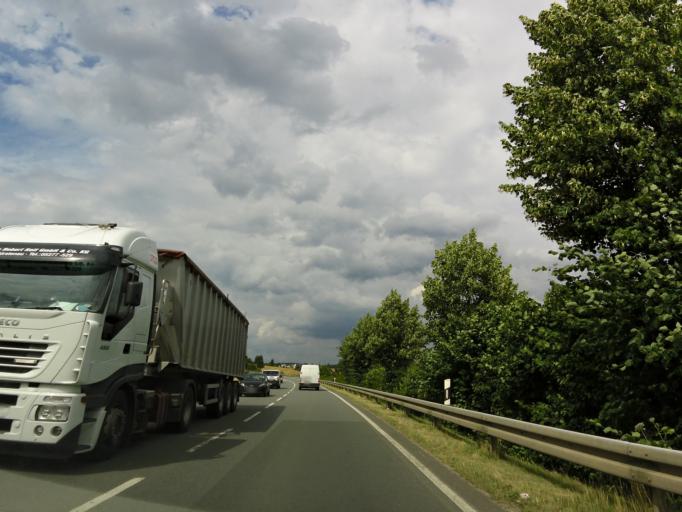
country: DE
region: North Rhine-Westphalia
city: Beverungen
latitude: 51.6850
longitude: 9.3778
